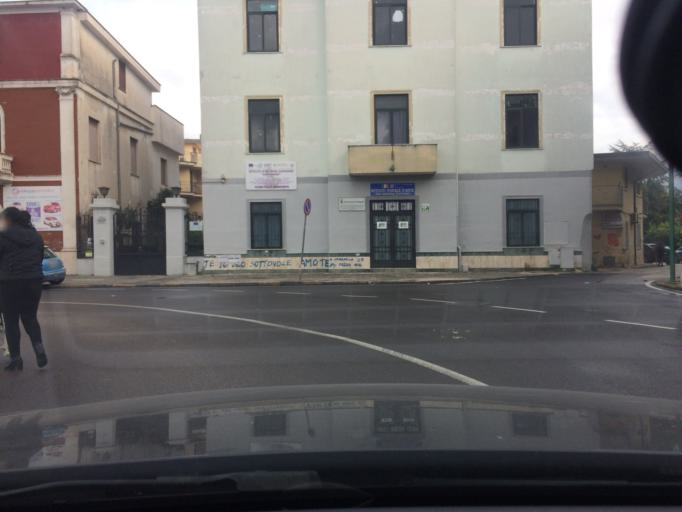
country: IT
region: Campania
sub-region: Provincia di Napoli
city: San Gennaro Vesuviano
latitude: 40.8603
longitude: 14.5300
